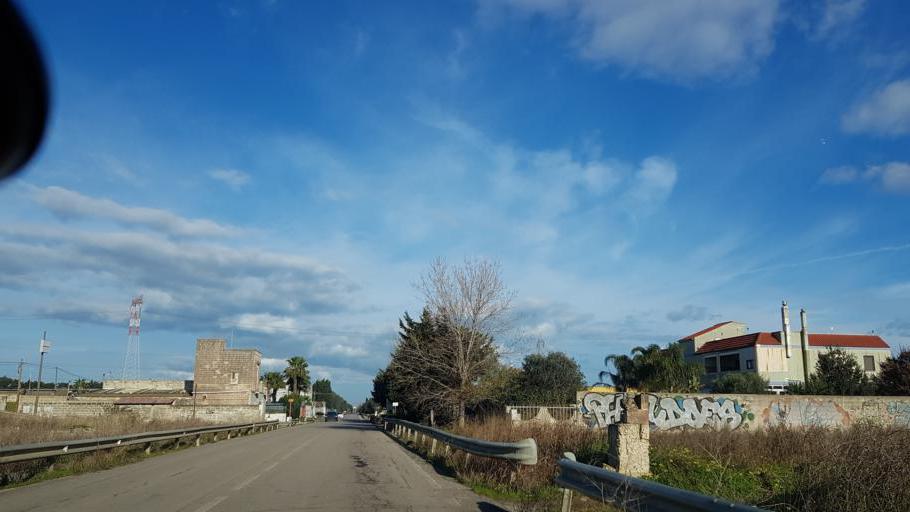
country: IT
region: Apulia
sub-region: Provincia di Brindisi
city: La Rosa
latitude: 40.6008
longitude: 17.9570
